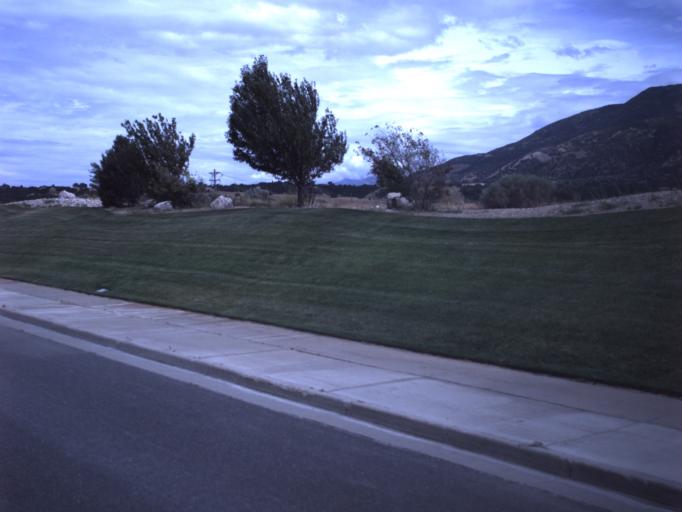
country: US
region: Utah
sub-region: Davis County
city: South Weber
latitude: 41.1281
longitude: -111.9222
